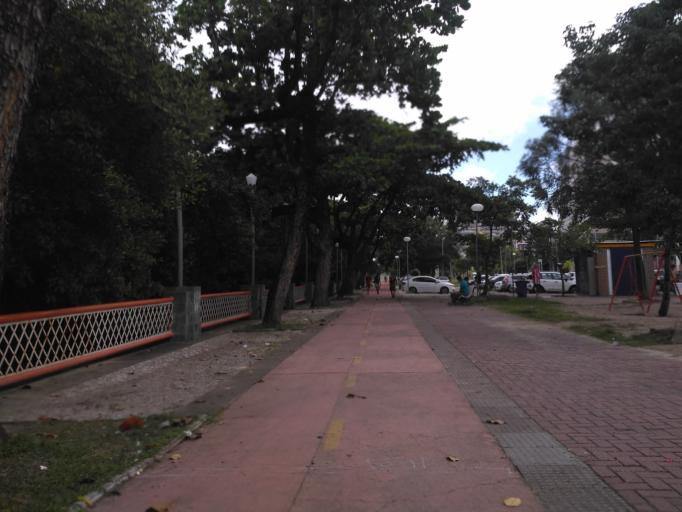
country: BR
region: Pernambuco
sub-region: Recife
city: Recife
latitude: -8.0552
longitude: -34.8768
